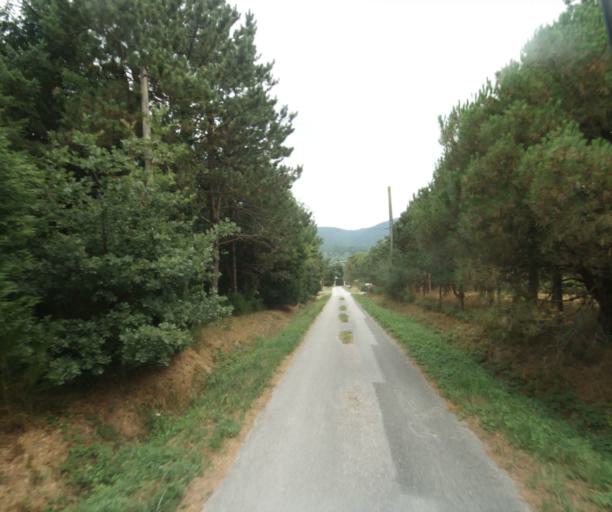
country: FR
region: Midi-Pyrenees
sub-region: Departement de la Haute-Garonne
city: Revel
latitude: 43.4382
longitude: 2.0133
